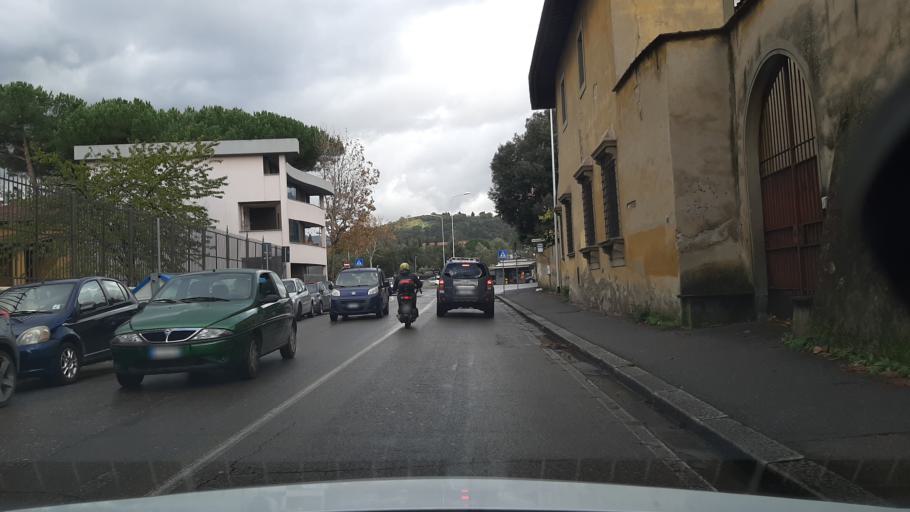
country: IT
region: Tuscany
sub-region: Province of Florence
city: Florence
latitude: 43.8020
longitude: 11.2471
